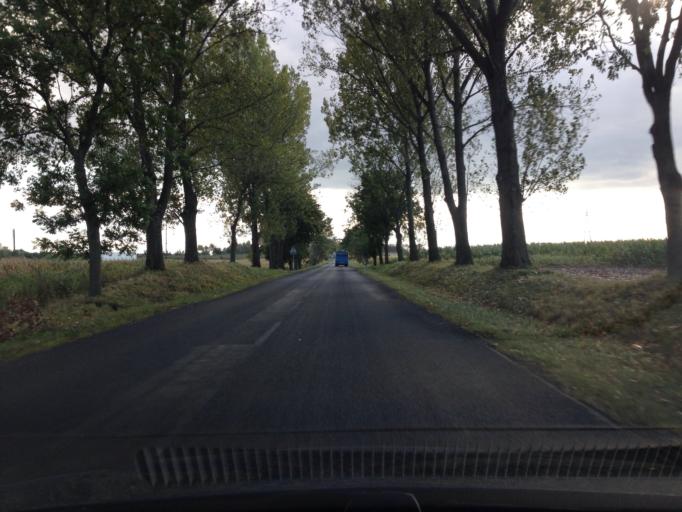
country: PL
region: Kujawsko-Pomorskie
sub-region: Powiat rypinski
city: Rogowo
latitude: 53.0242
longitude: 19.3539
